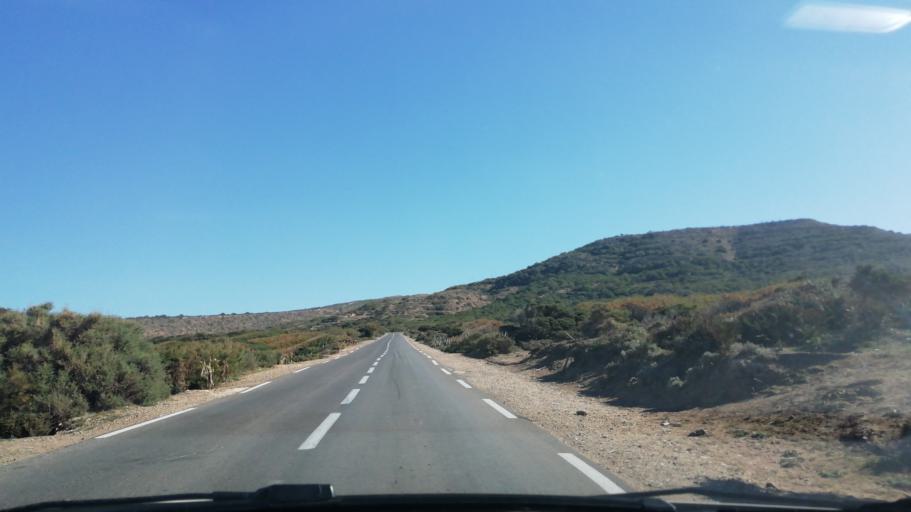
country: DZ
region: Ain Temouchent
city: El Amria
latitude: 35.6432
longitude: -1.0569
